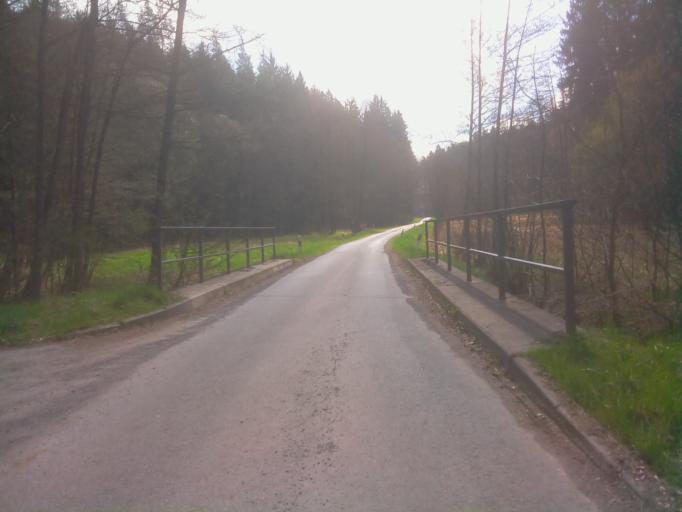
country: DE
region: Thuringia
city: Trockenborn-Wolfersdorf
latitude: 50.7871
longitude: 11.7133
